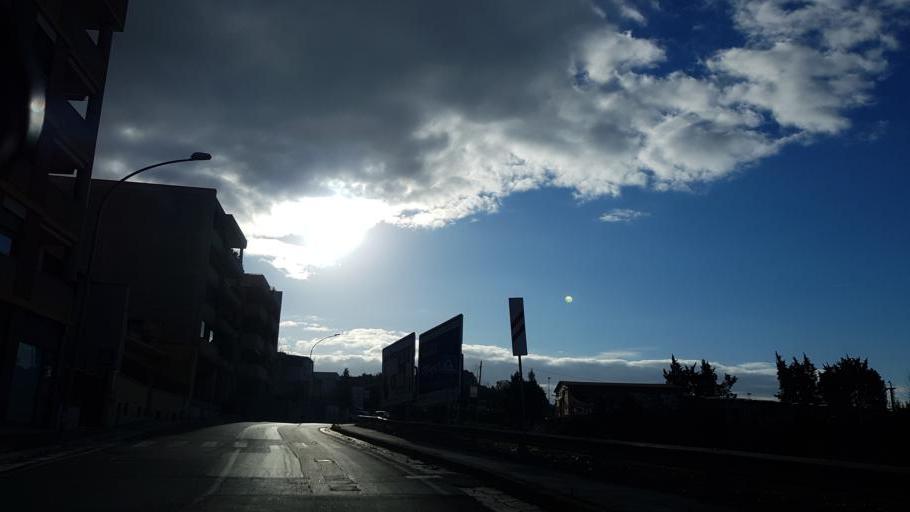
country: IT
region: Apulia
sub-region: Provincia di Brindisi
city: Brindisi
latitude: 40.6299
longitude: 17.9459
